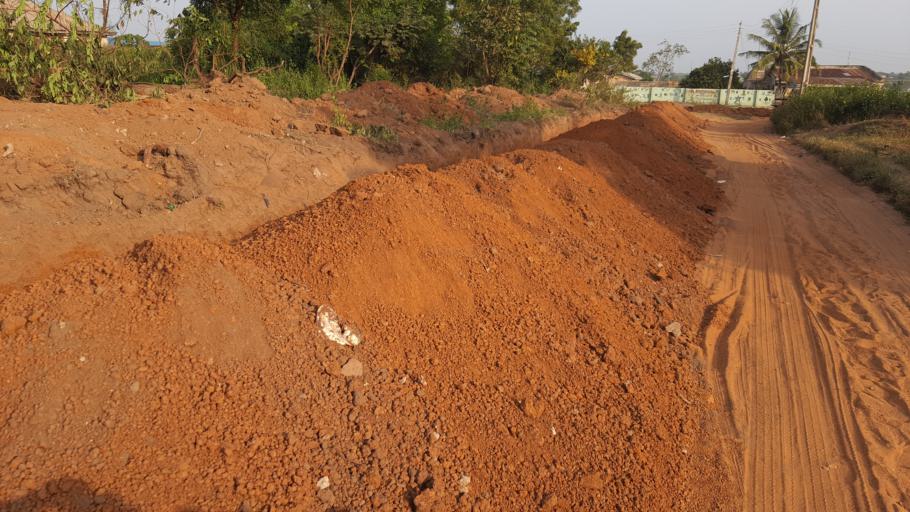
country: NG
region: Osun
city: Iwo
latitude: 7.6219
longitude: 4.1596
